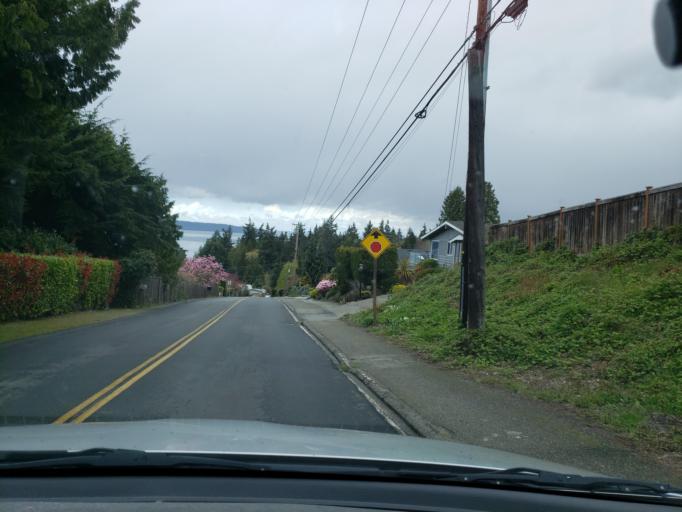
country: US
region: Washington
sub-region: Snohomish County
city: Meadowdale
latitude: 47.8339
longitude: -122.3522
